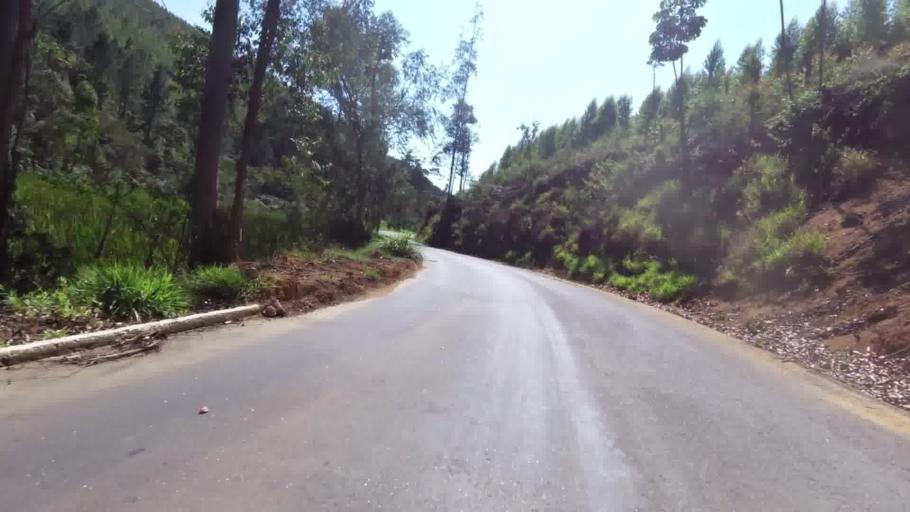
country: BR
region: Espirito Santo
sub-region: Marechal Floriano
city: Marechal Floriano
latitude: -20.4413
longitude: -40.8829
